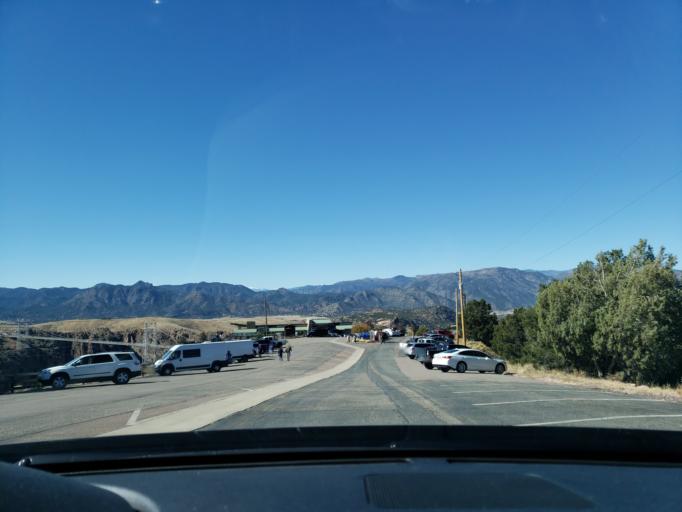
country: US
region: Colorado
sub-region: Fremont County
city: Canon City
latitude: 38.4633
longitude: -105.3190
